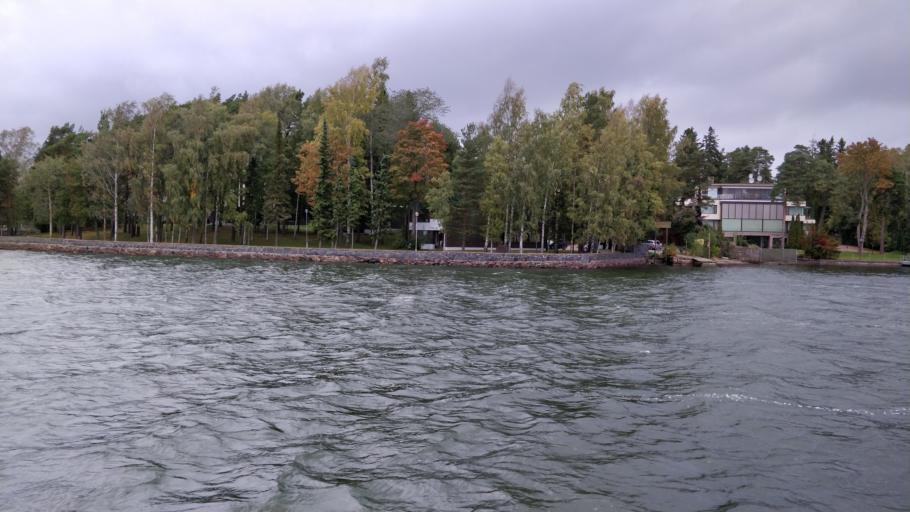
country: FI
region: Uusimaa
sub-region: Helsinki
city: Helsinki
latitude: 60.1790
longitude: 25.0183
